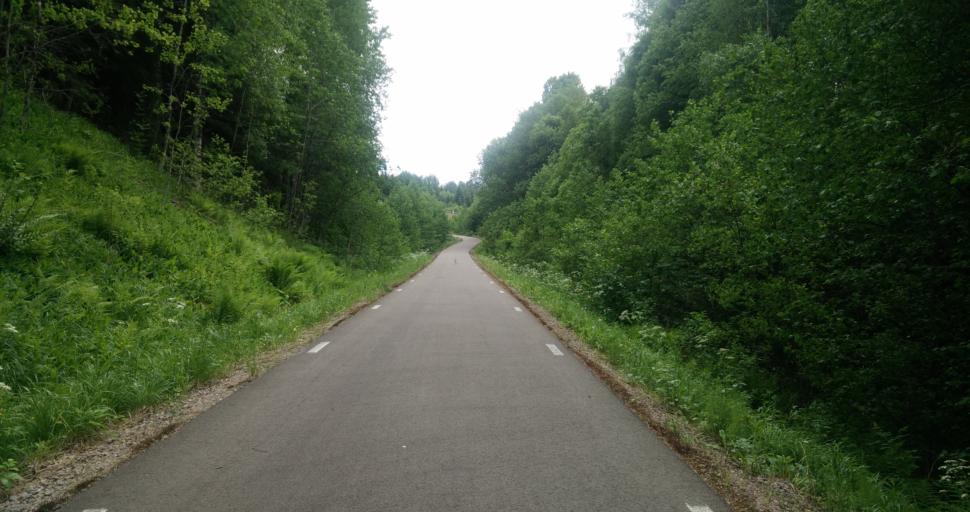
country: SE
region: Vaermland
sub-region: Hagfors Kommun
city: Hagfors
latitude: 59.9892
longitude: 13.5856
